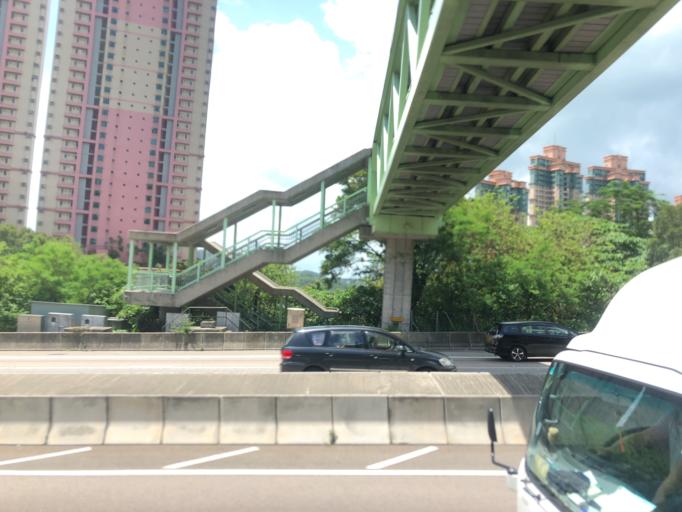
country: HK
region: Tsuen Wan
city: Tsuen Wan
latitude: 22.3668
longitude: 114.0541
